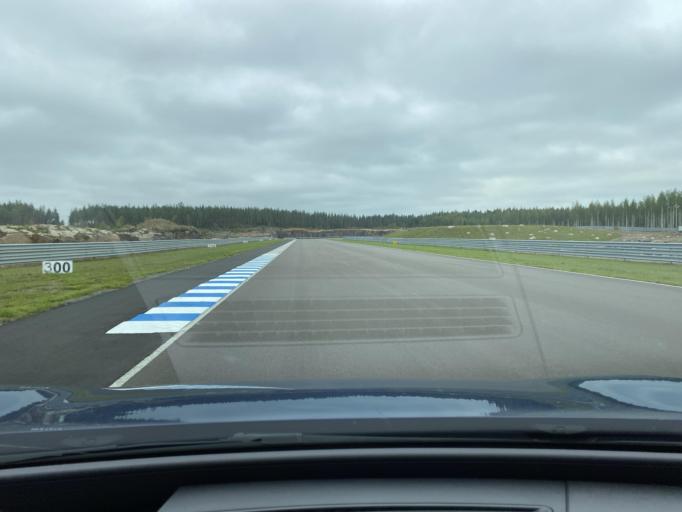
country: FI
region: Kymenlaakso
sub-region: Kouvola
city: Iitti
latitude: 60.8800
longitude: 26.4737
